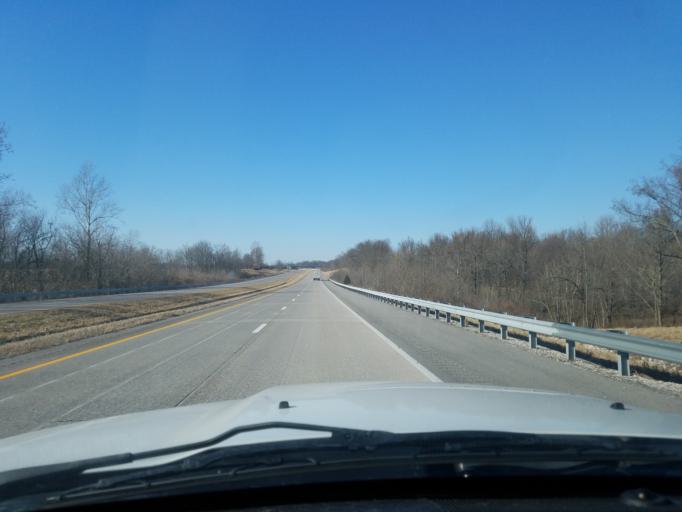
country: US
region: Indiana
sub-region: Warrick County
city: Newburgh
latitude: 37.7639
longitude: -87.4209
